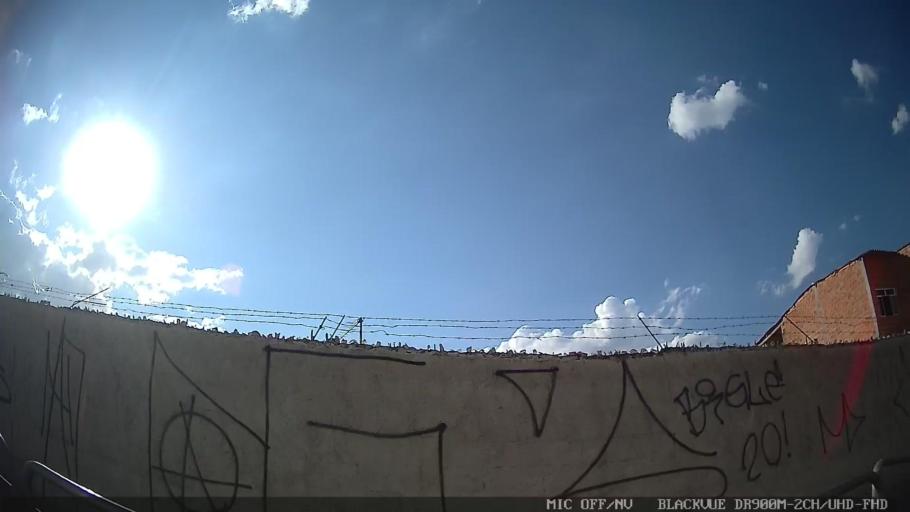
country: BR
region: Sao Paulo
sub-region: Ferraz De Vasconcelos
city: Ferraz de Vasconcelos
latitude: -23.5304
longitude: -46.4482
